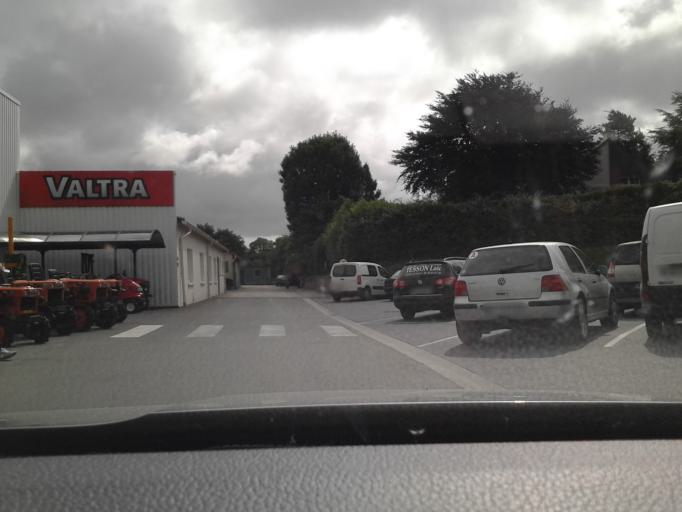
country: FR
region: Lower Normandy
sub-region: Departement de la Manche
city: Valognes
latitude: 49.5032
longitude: -1.4597
